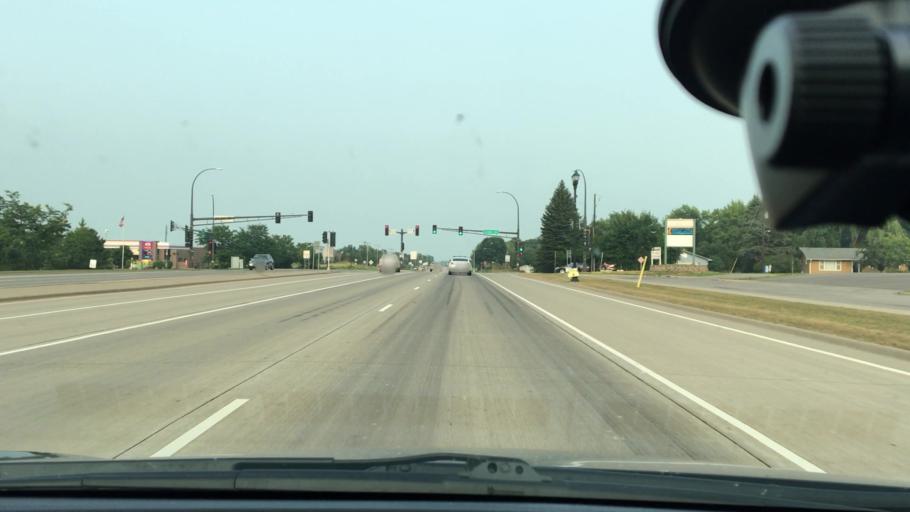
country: US
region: Minnesota
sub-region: Wright County
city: Saint Michael
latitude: 45.2102
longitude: -93.6487
